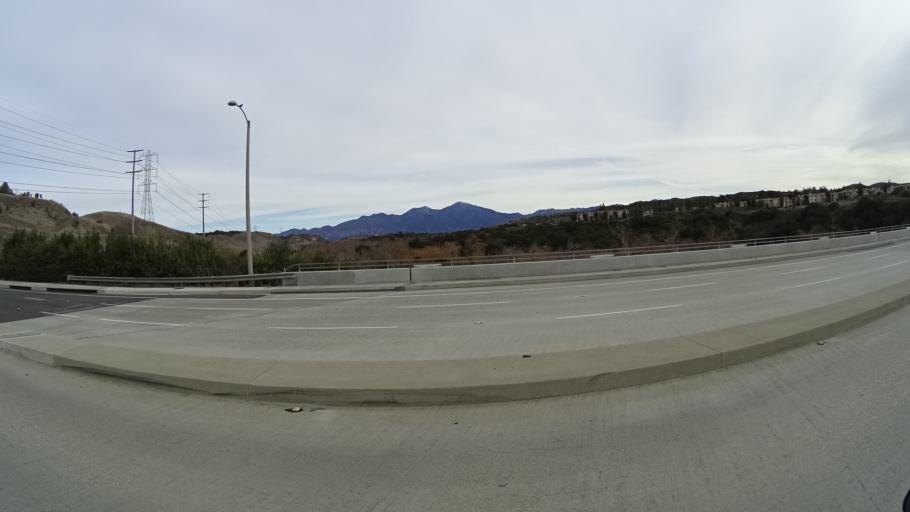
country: US
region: California
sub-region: Orange County
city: Las Flores
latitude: 33.5852
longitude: -117.6369
